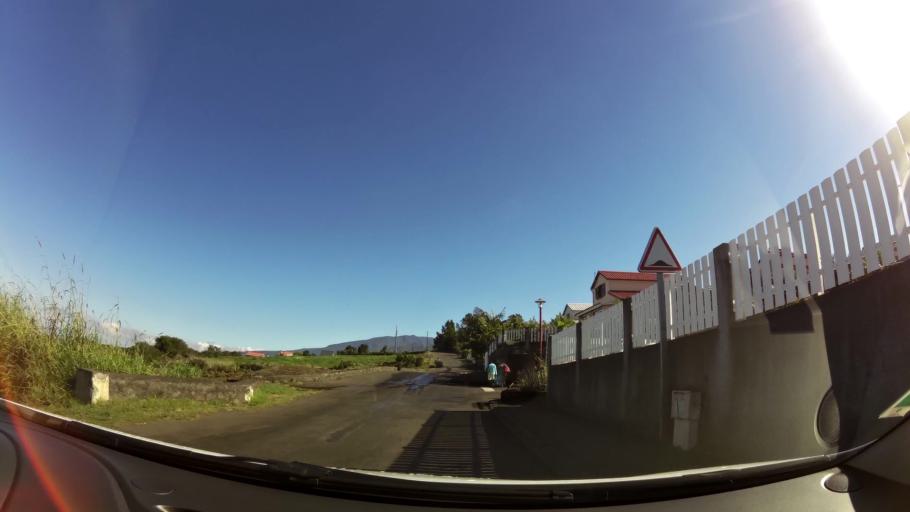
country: RE
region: Reunion
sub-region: Reunion
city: Le Tampon
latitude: -21.2365
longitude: 55.5245
